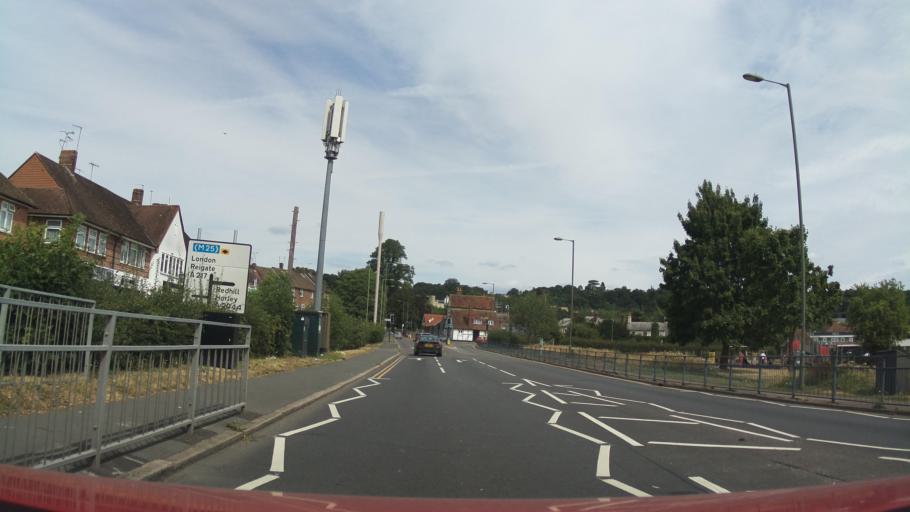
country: GB
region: England
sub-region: Surrey
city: Reigate
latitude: 51.2230
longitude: -0.1991
